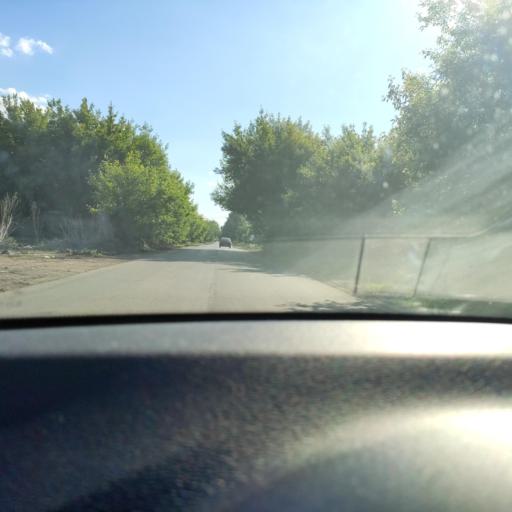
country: RU
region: Samara
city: Smyshlyayevka
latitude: 53.2446
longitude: 50.3614
